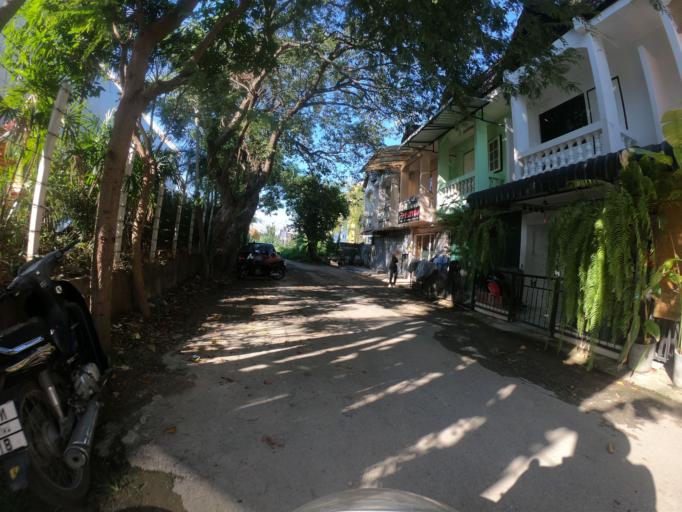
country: TH
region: Chiang Mai
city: Chiang Mai
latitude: 18.8079
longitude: 98.9786
